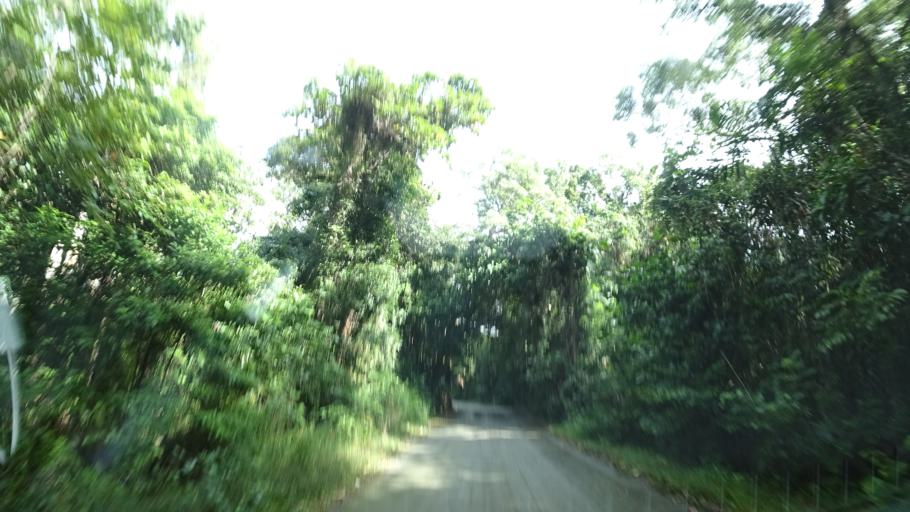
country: AU
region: Queensland
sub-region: Cairns
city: Port Douglas
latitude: -16.0960
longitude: 145.4637
